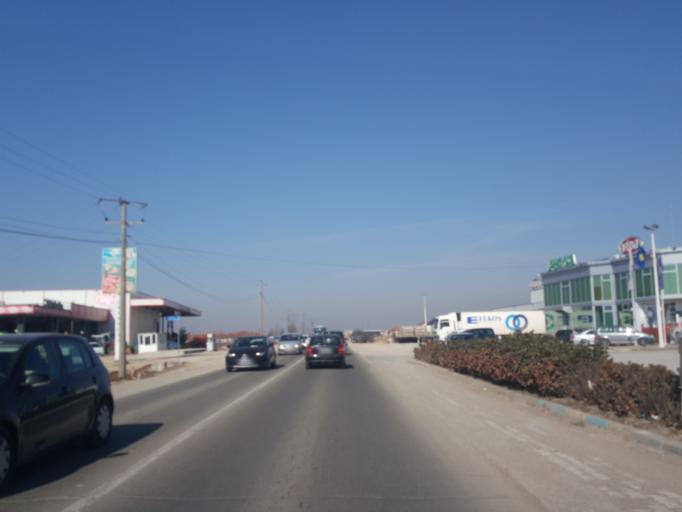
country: XK
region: Mitrovica
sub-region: Vushtrri
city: Vushtrri
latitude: 42.7839
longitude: 21.0105
